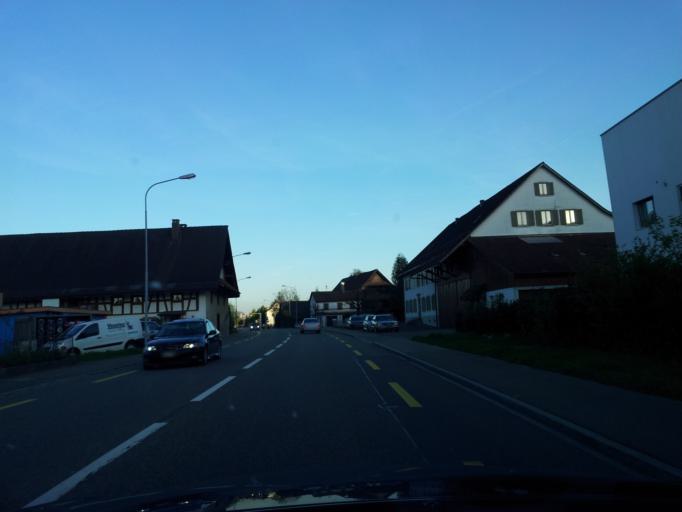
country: CH
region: Aargau
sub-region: Bezirk Baden
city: Killwangen
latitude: 47.4351
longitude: 8.3461
